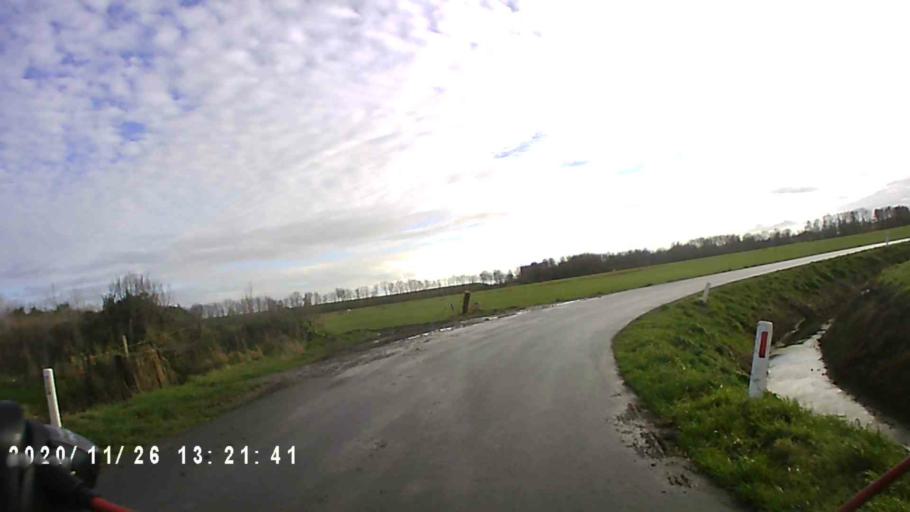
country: NL
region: Groningen
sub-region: Gemeente Delfzijl
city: Delfzijl
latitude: 53.3476
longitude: 6.8928
